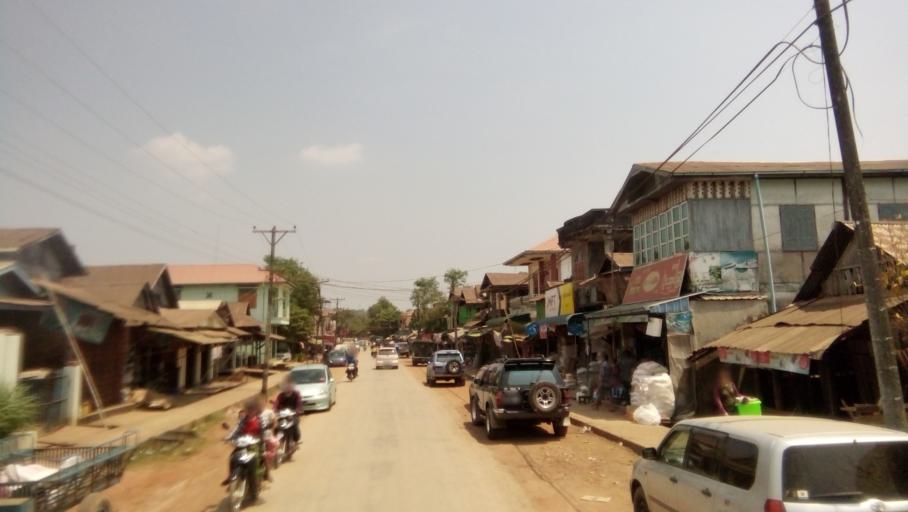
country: MM
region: Kayin
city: Hpa-an
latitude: 17.1253
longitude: 97.8183
